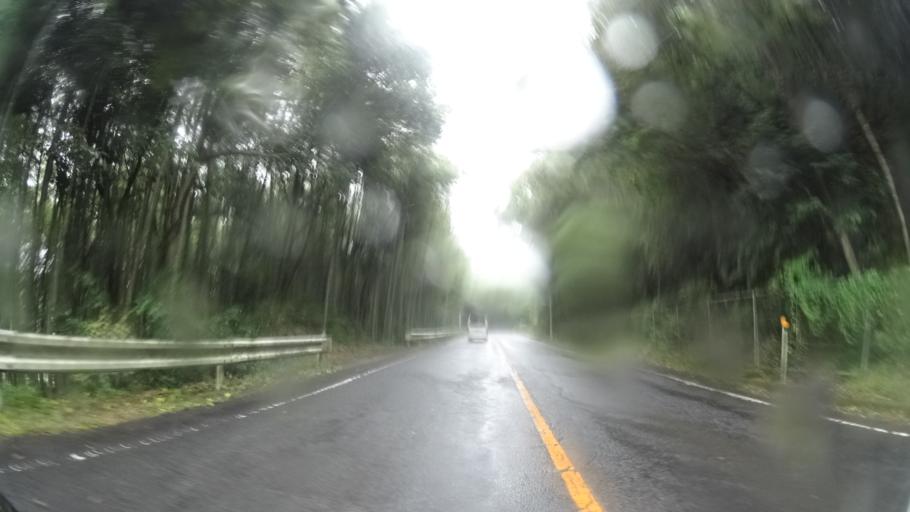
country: JP
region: Kagoshima
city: Kajiki
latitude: 31.8997
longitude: 130.7007
